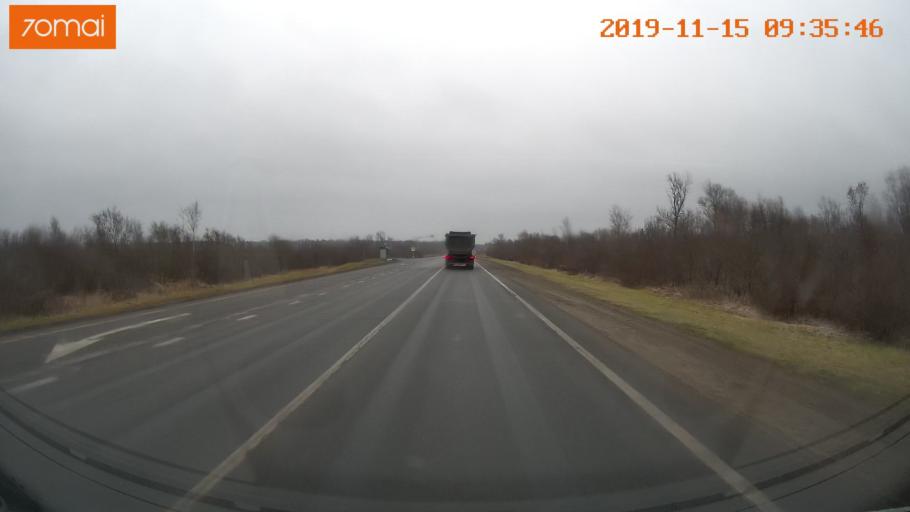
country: RU
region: Vologda
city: Sheksna
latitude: 59.2524
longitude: 38.4061
